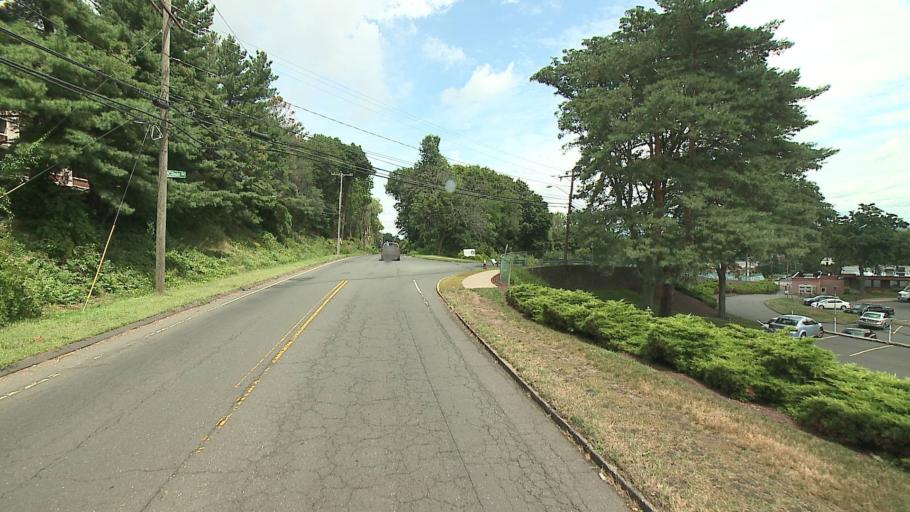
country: US
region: Connecticut
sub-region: Hartford County
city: New Britain
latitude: 41.6480
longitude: -72.7882
